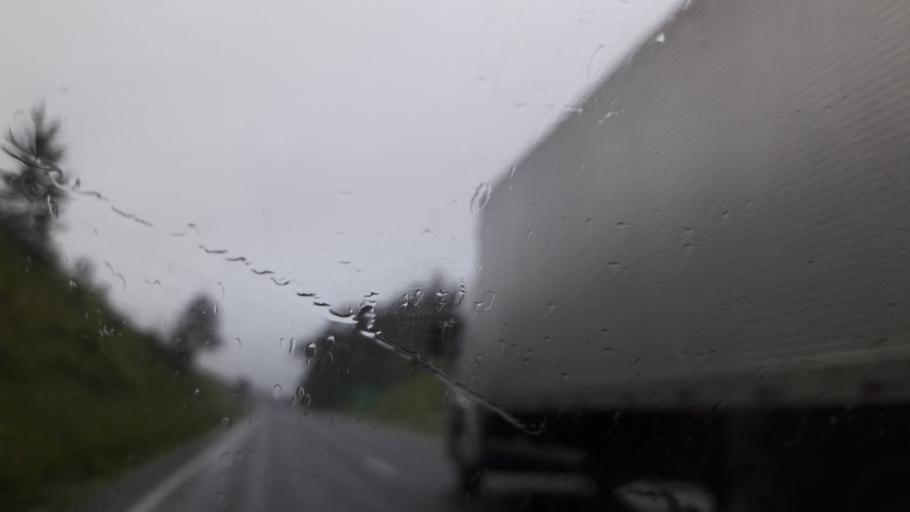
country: BR
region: Parana
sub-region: Campina Grande Do Sul
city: Campina Grande do Sul
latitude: -25.1082
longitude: -48.7940
